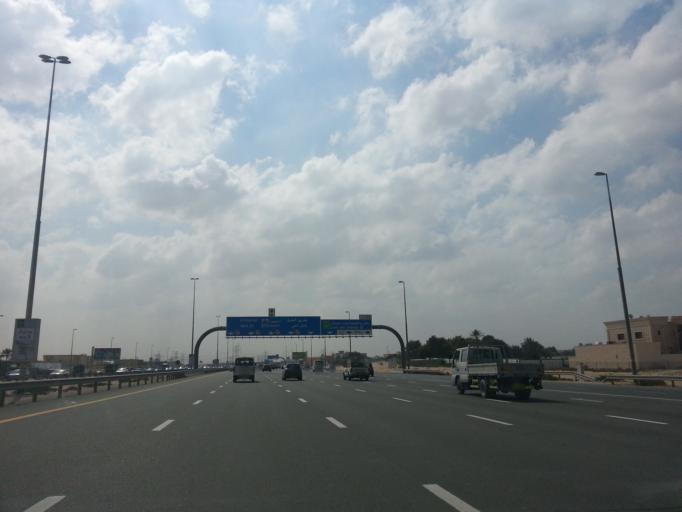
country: AE
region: Dubai
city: Dubai
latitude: 25.1571
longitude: 55.2614
